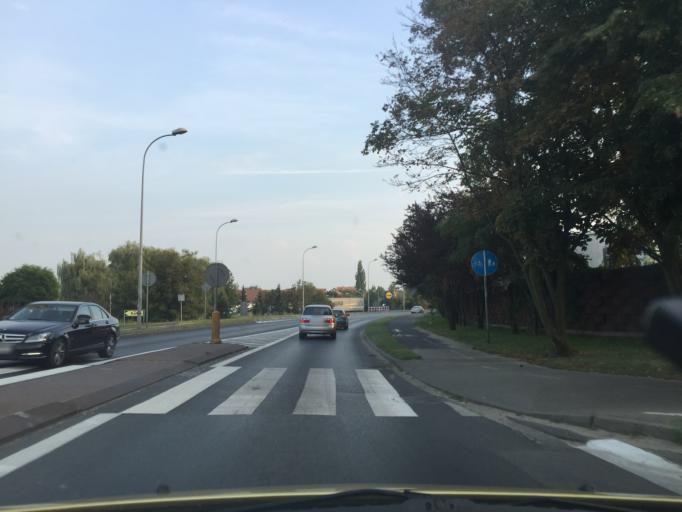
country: PL
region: Greater Poland Voivodeship
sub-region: Powiat jarocinski
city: Jarocin
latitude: 51.9707
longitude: 17.5059
